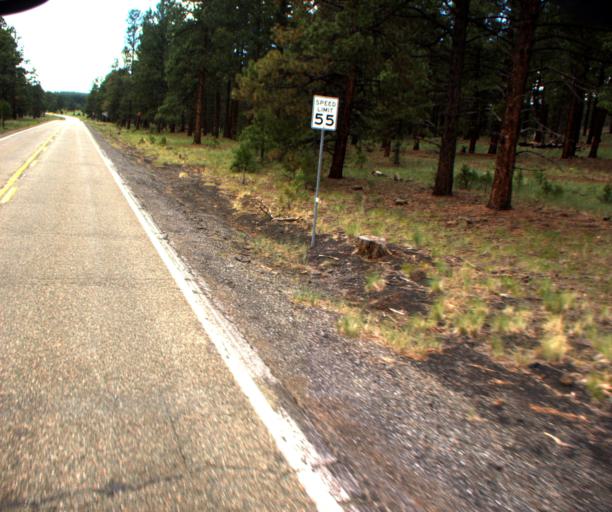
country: US
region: Arizona
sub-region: Coconino County
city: Parks
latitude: 35.3815
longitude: -111.7830
